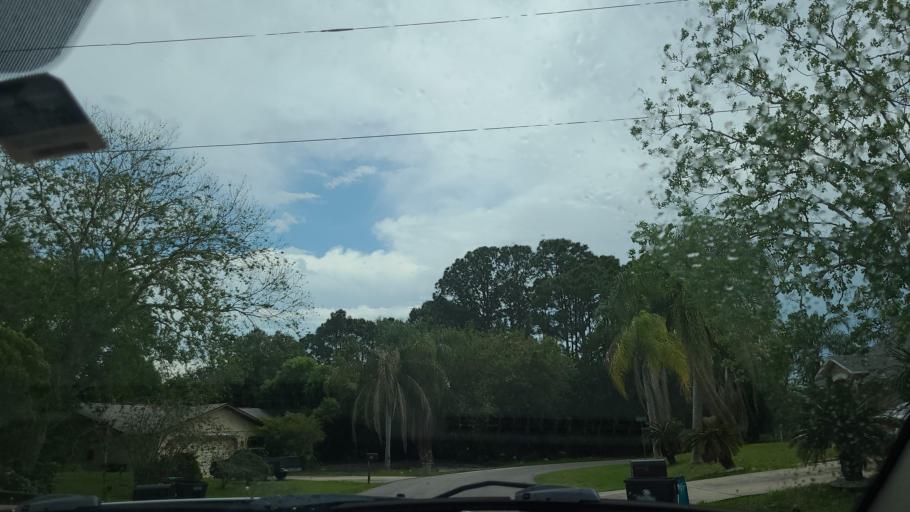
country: US
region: Florida
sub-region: Brevard County
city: Grant-Valkaria
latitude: 27.9468
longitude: -80.6412
